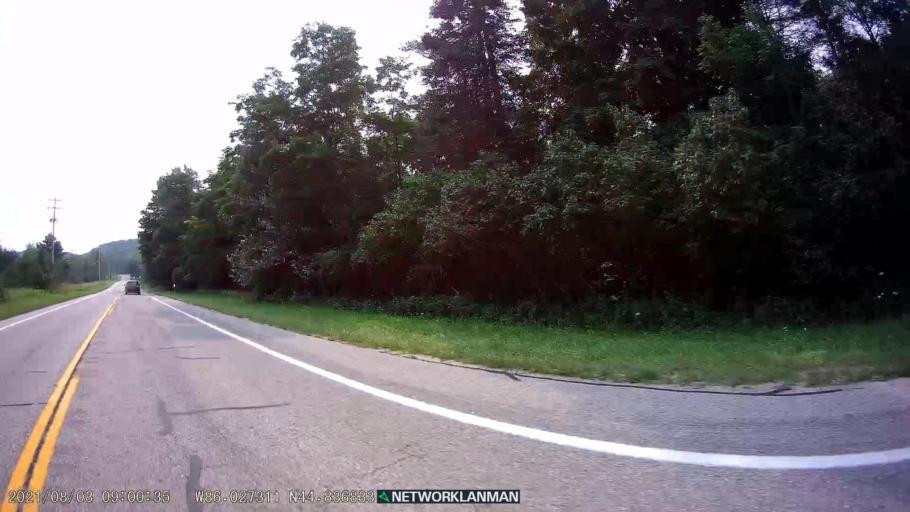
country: US
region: Michigan
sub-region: Benzie County
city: Beulah
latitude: 44.8368
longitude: -86.0277
